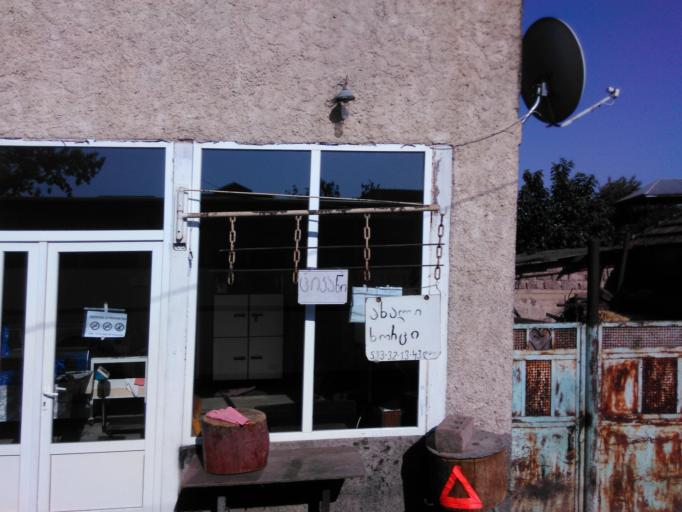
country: GE
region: Shida Kartli
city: Kaspi
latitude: 41.9338
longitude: 44.5763
